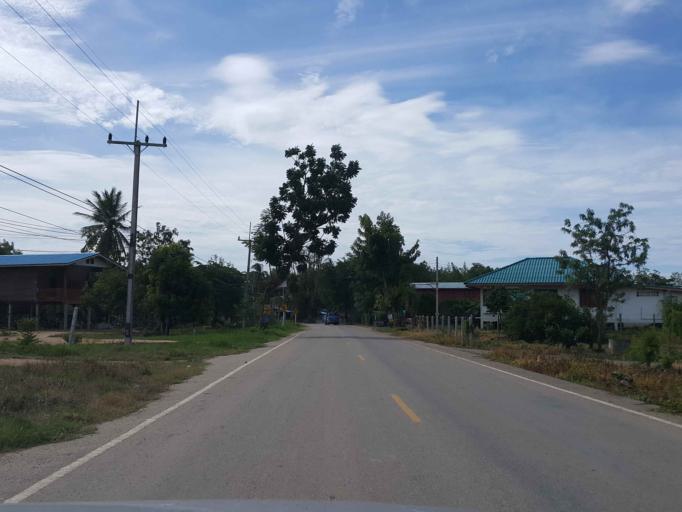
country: TH
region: Sukhothai
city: Ban Dan Lan Hoi
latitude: 17.1180
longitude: 99.5347
